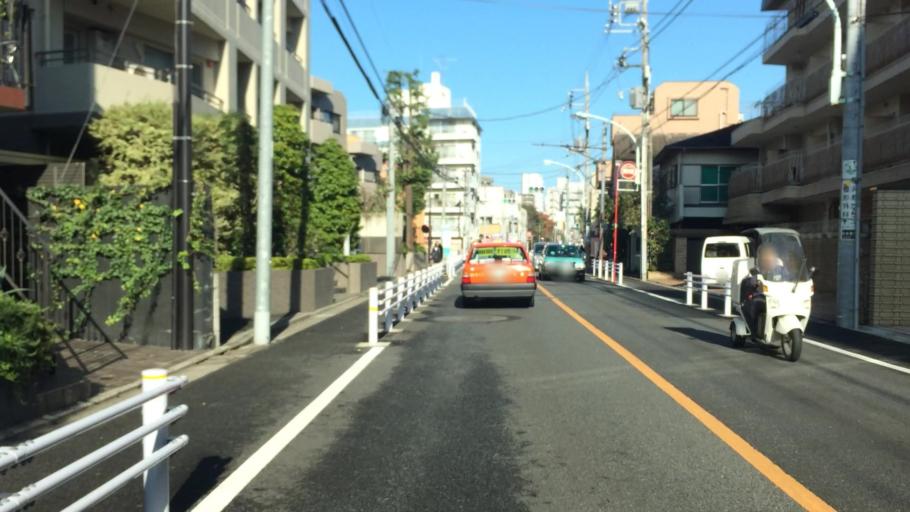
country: JP
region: Tokyo
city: Tokyo
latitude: 35.6289
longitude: 139.6633
